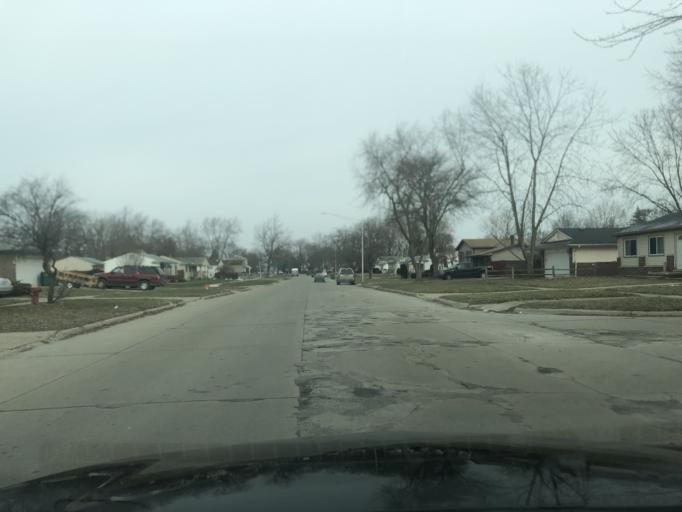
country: US
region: Michigan
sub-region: Wayne County
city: Taylor
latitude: 42.1916
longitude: -83.3158
